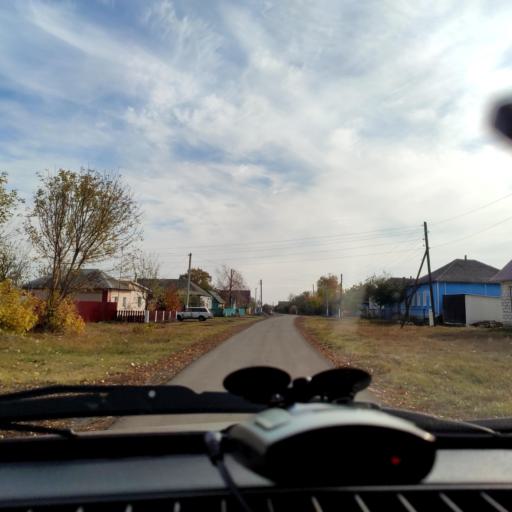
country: RU
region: Voronezj
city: Rossosh'
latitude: 51.1997
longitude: 38.7660
